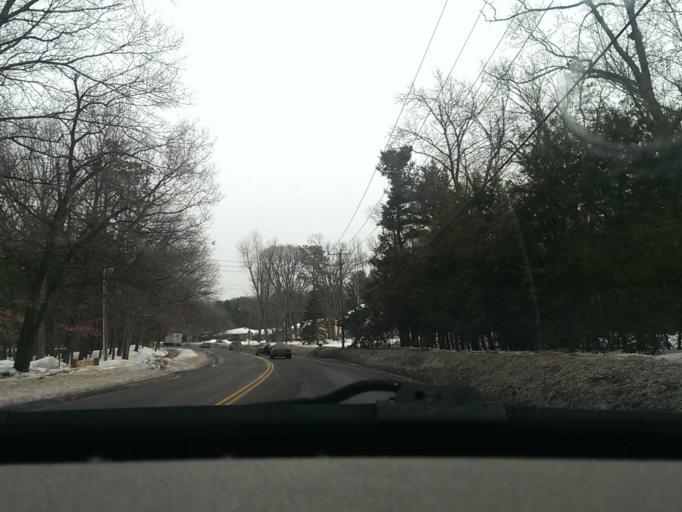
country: US
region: Massachusetts
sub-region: Hampden County
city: Longmeadow
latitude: 42.0627
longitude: -72.5511
